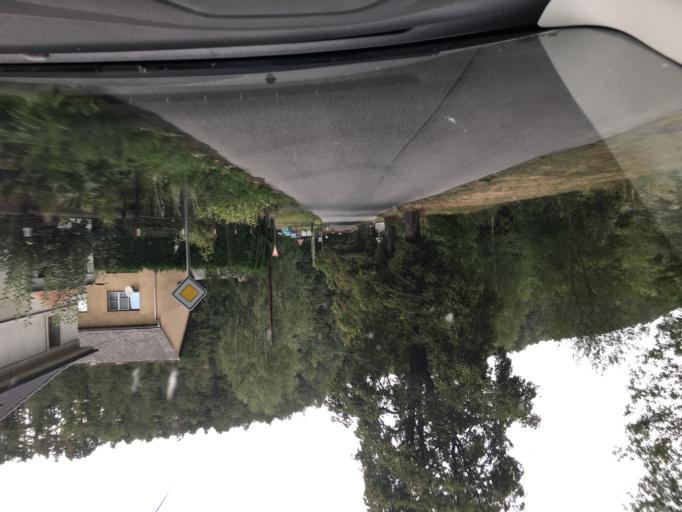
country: CZ
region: Ustecky
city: Ceska Kamenice
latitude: 50.8064
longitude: 14.3598
